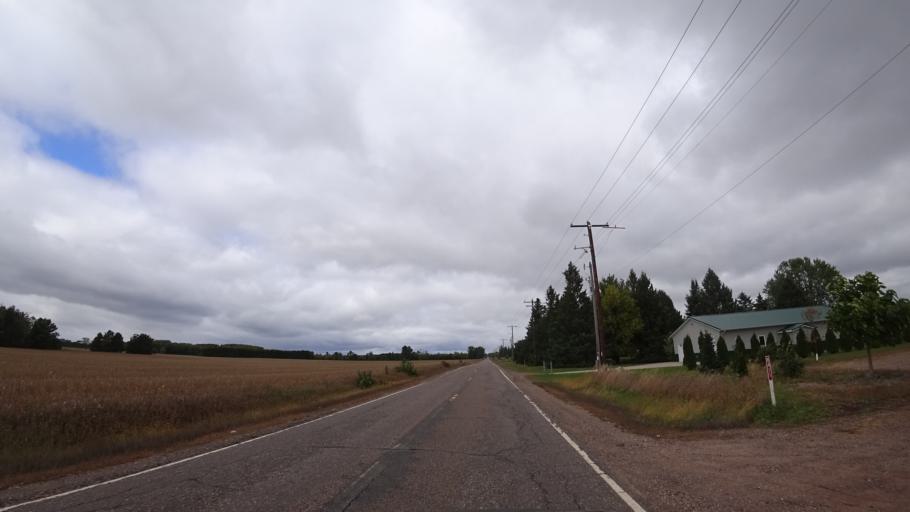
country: US
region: Wisconsin
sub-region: Chippewa County
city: Lake Wissota
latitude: 44.9646
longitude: -91.2678
